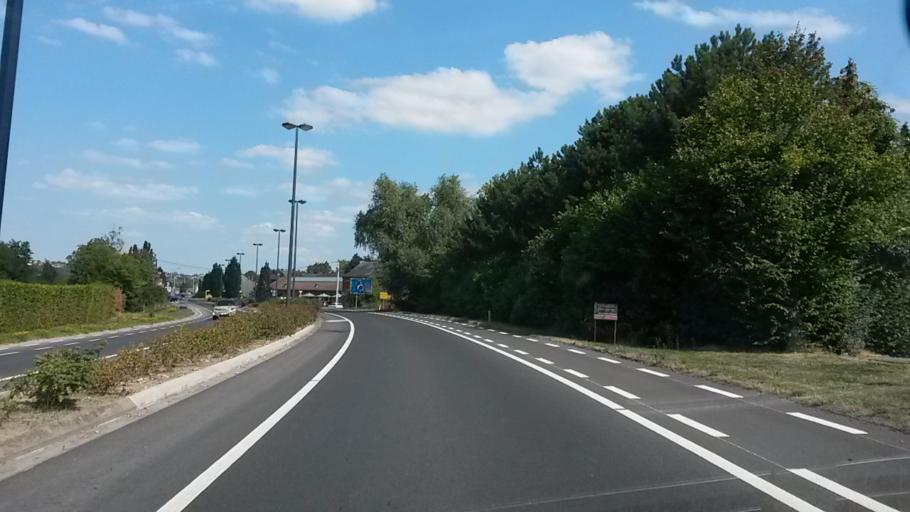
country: BE
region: Wallonia
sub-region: Province de Namur
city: Floreffe
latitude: 50.4414
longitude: 4.7916
